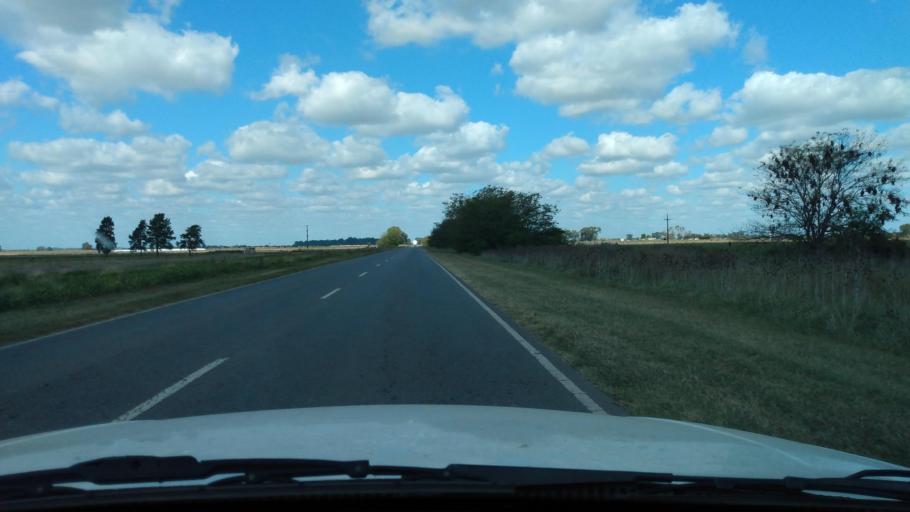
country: AR
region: Buenos Aires
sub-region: Partido de Navarro
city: Navarro
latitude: -34.9686
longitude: -59.3176
